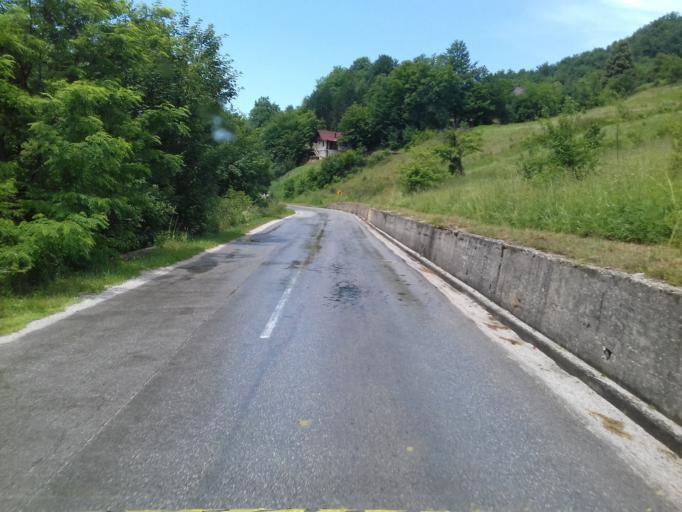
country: BA
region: Federation of Bosnia and Herzegovina
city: Kiseljak
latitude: 43.9502
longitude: 18.0948
